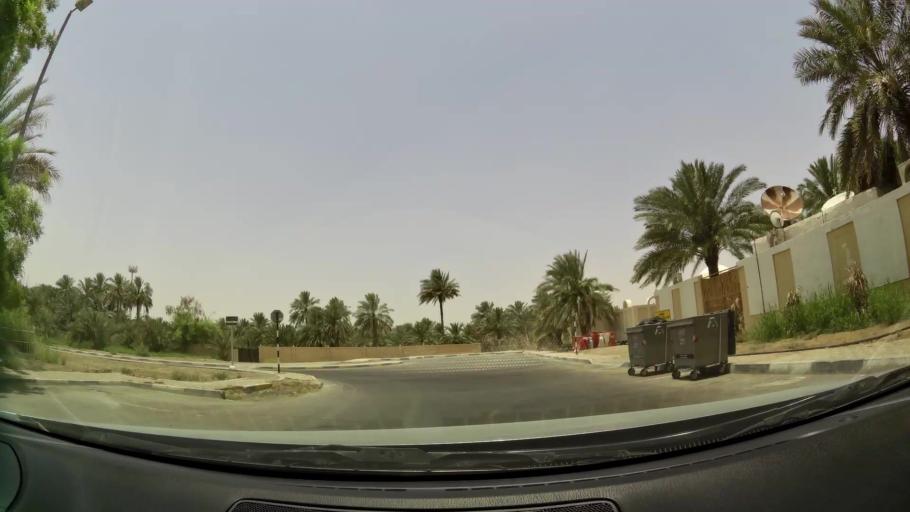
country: AE
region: Abu Dhabi
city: Al Ain
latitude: 24.2081
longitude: 55.7442
